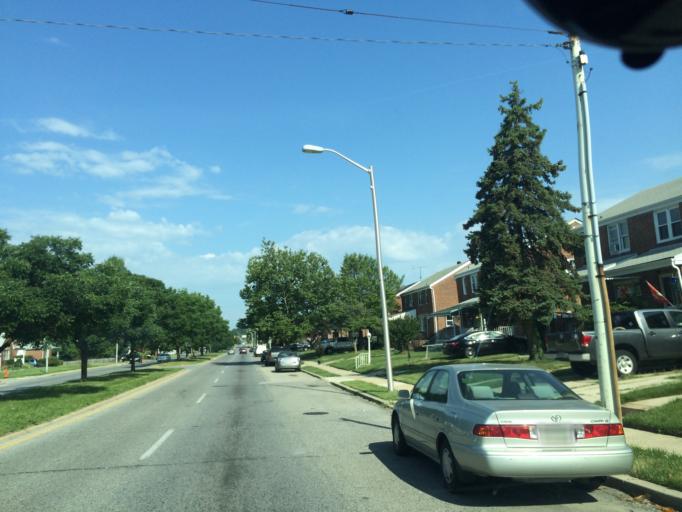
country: US
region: Maryland
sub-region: Baltimore County
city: Parkville
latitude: 39.3599
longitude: -76.5422
